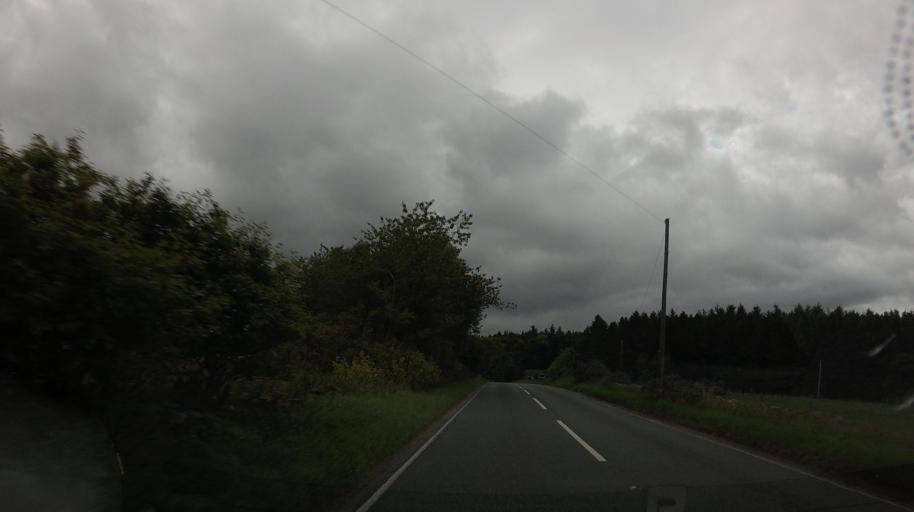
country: GB
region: Scotland
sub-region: Aberdeenshire
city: Kemnay
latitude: 57.1851
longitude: -2.5418
